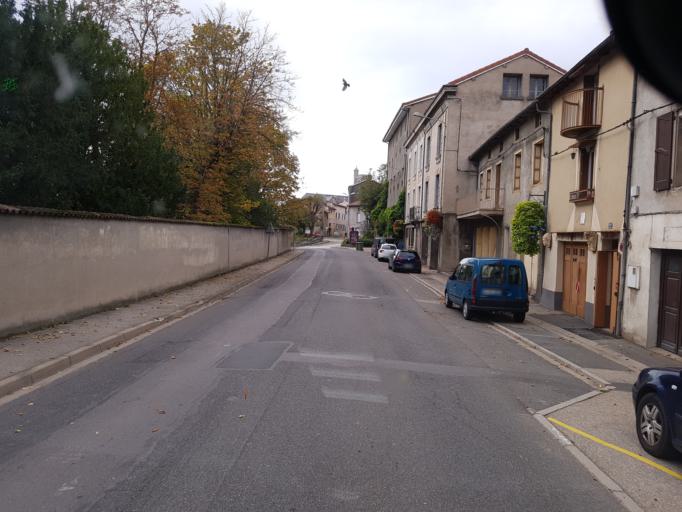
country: FR
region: Rhone-Alpes
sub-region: Departement de la Loire
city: Saint-Galmier
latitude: 45.5929
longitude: 4.3204
